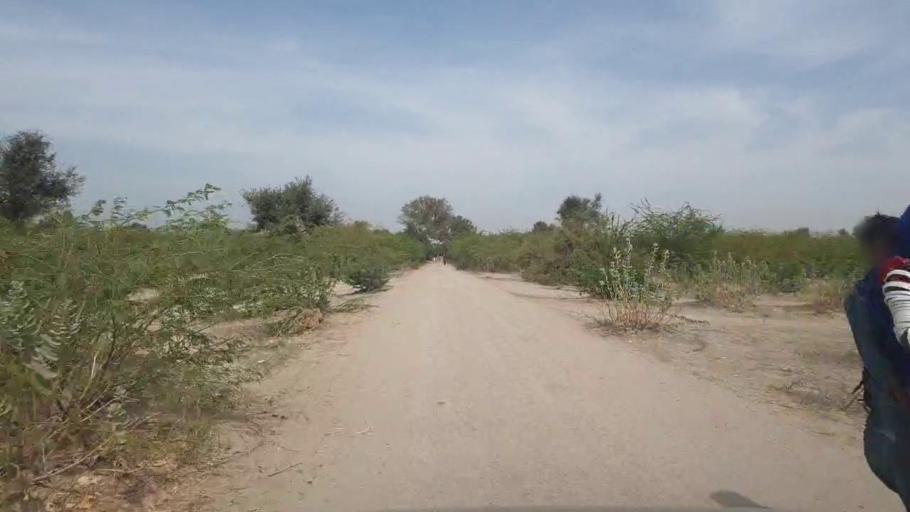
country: PK
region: Sindh
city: Umarkot
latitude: 25.2576
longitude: 69.7243
